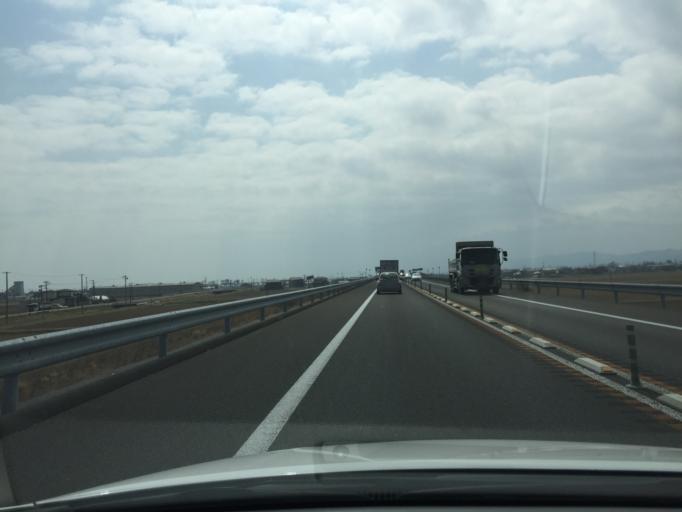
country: JP
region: Miyagi
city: Watari
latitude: 38.0504
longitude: 140.8937
